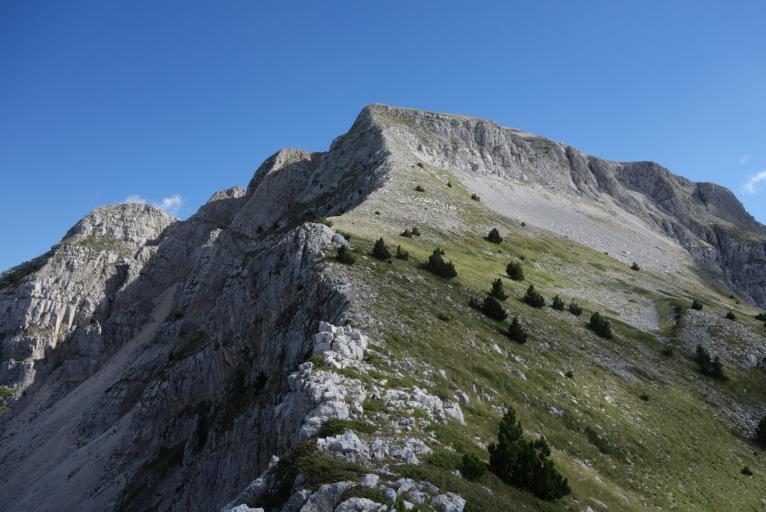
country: AL
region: Berat
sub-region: Rrethi i Beratit
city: Polican
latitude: 40.6448
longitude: 20.1587
